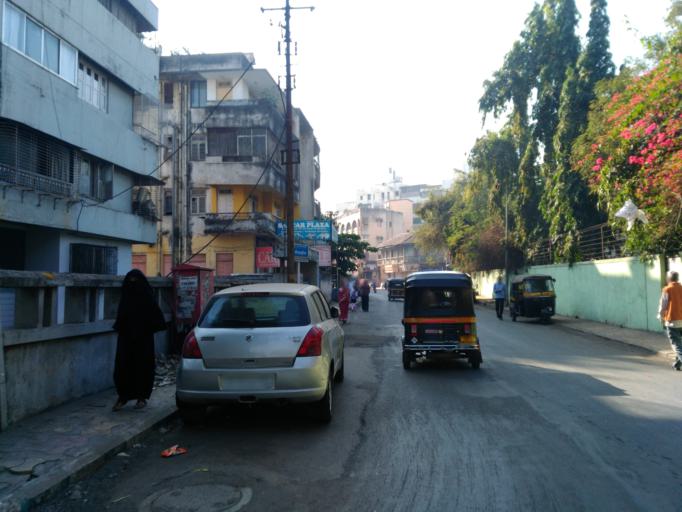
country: IN
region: Maharashtra
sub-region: Pune Division
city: Pune
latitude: 18.5112
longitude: 73.8719
